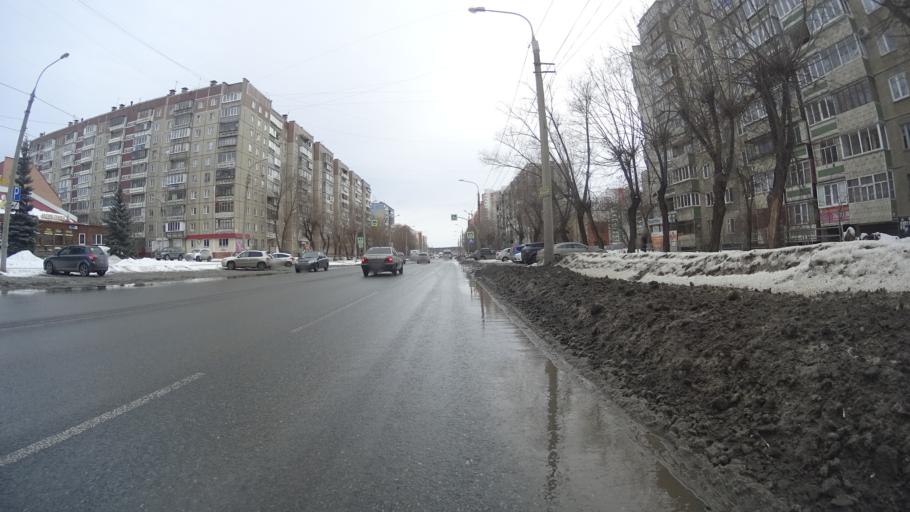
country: RU
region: Chelyabinsk
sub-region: Gorod Chelyabinsk
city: Chelyabinsk
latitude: 55.1790
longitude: 61.3084
